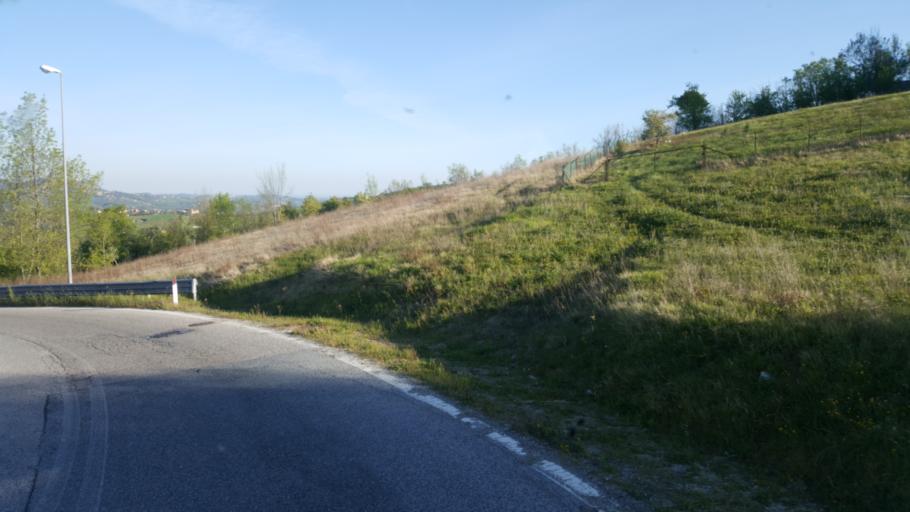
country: SM
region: Borgo Maggiore
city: Borgo Maggiore
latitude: 43.9452
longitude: 12.4369
